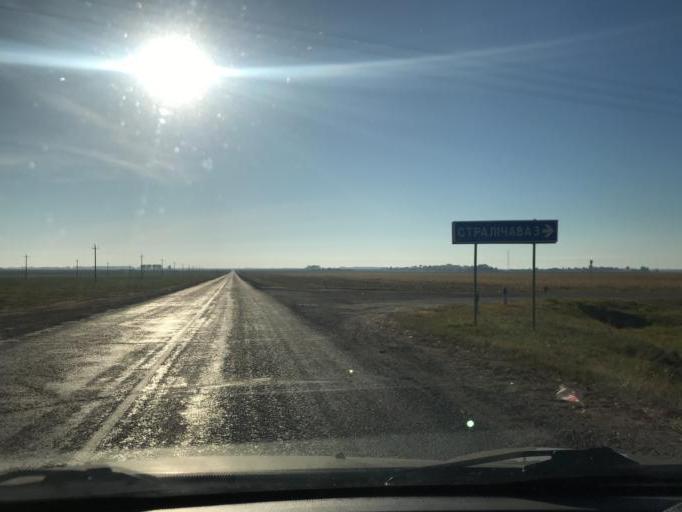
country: BY
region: Gomel
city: Khoyniki
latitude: 51.8495
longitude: 30.0236
